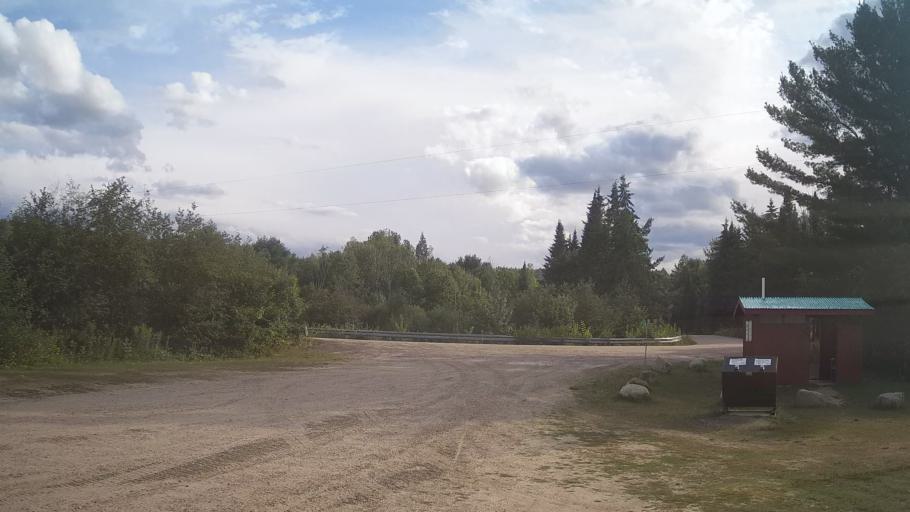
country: CA
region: Ontario
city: Mattawa
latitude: 46.2530
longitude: -78.2877
